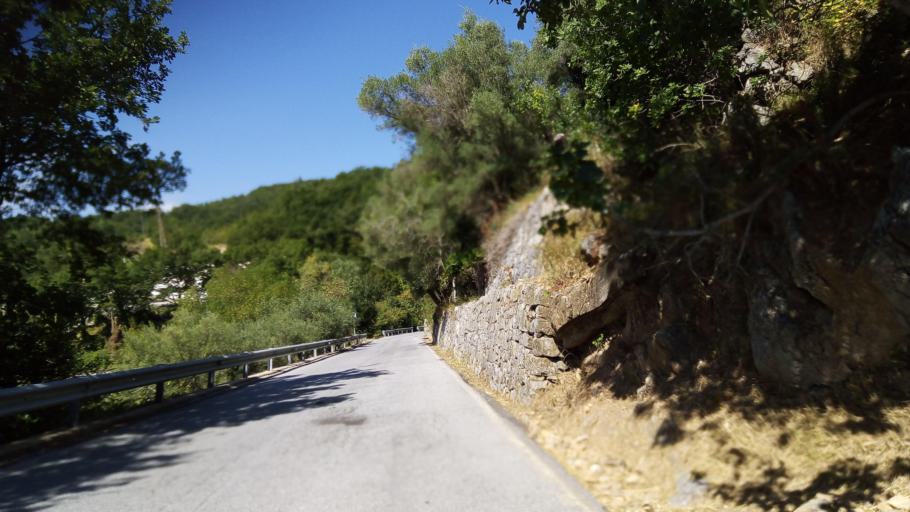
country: IT
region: Liguria
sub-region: Provincia di Savona
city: Balestrino
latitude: 44.1447
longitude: 8.1667
